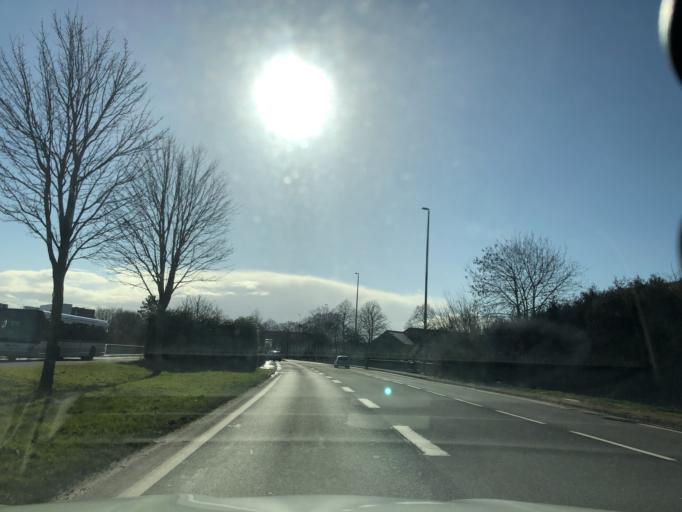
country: FR
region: Lower Normandy
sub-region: Departement du Calvados
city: Caen
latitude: 49.2031
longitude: -0.3528
